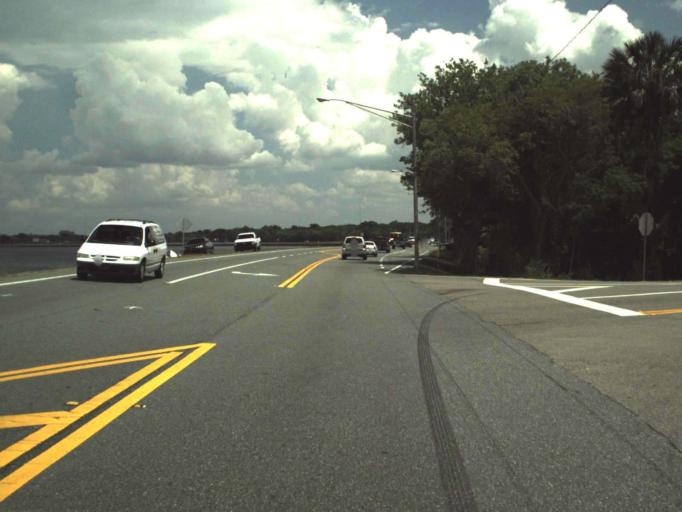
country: US
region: Florida
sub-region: Seminole County
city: Sanford
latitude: 28.8216
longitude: -81.2928
